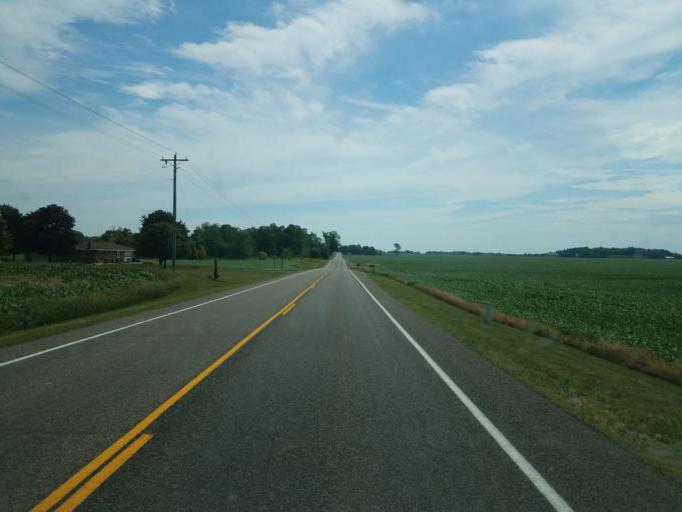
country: US
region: Michigan
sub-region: Eaton County
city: Charlotte
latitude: 42.6260
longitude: -84.8303
